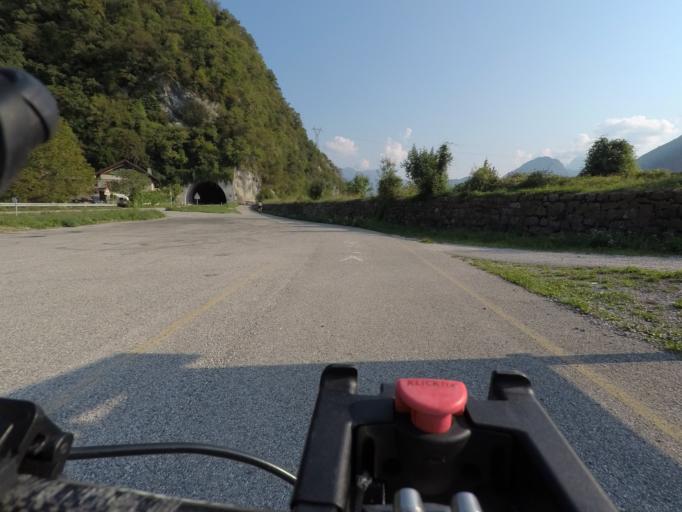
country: IT
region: Friuli Venezia Giulia
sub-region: Provincia di Udine
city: Tolmezzo
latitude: 46.4140
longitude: 13.0071
